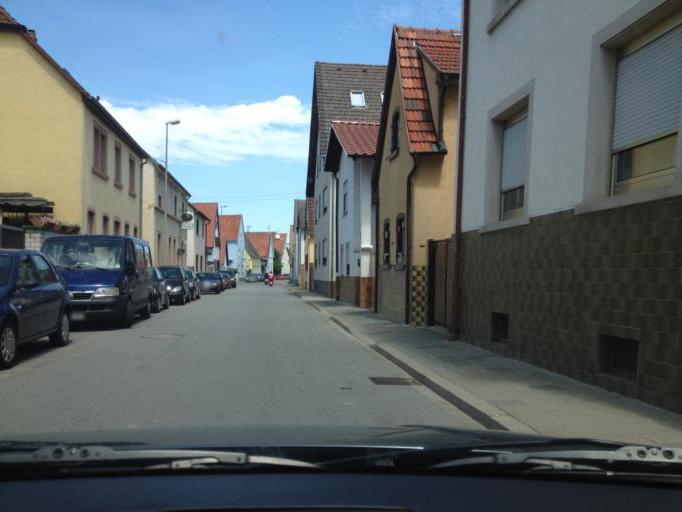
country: DE
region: Rheinland-Pfalz
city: Neuhofen
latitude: 49.4192
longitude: 8.4300
